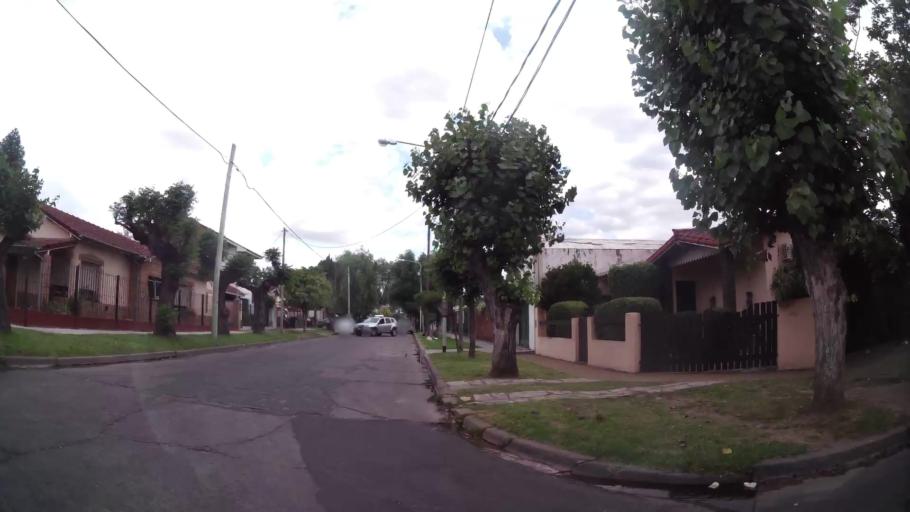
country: AR
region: Buenos Aires
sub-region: Partido de Tigre
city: Tigre
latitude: -34.4638
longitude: -58.6463
